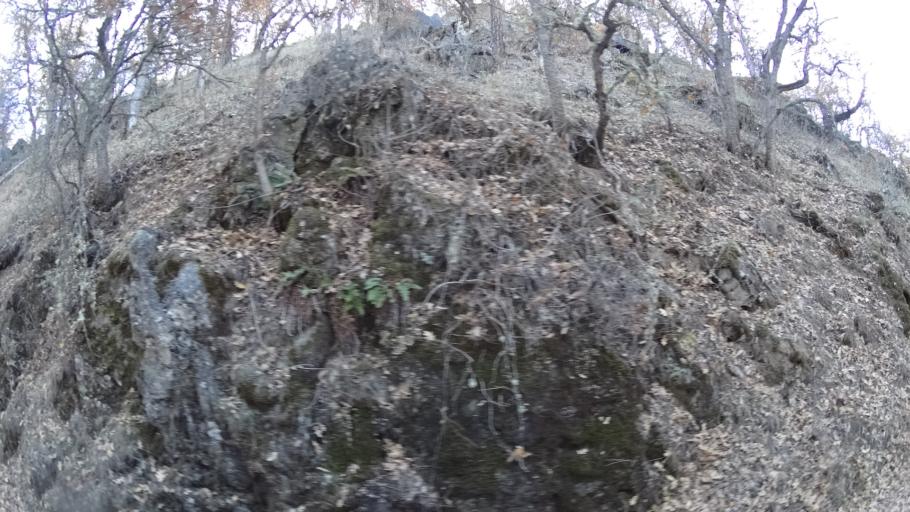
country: US
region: California
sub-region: Siskiyou County
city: Yreka
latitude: 41.8684
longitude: -122.8155
